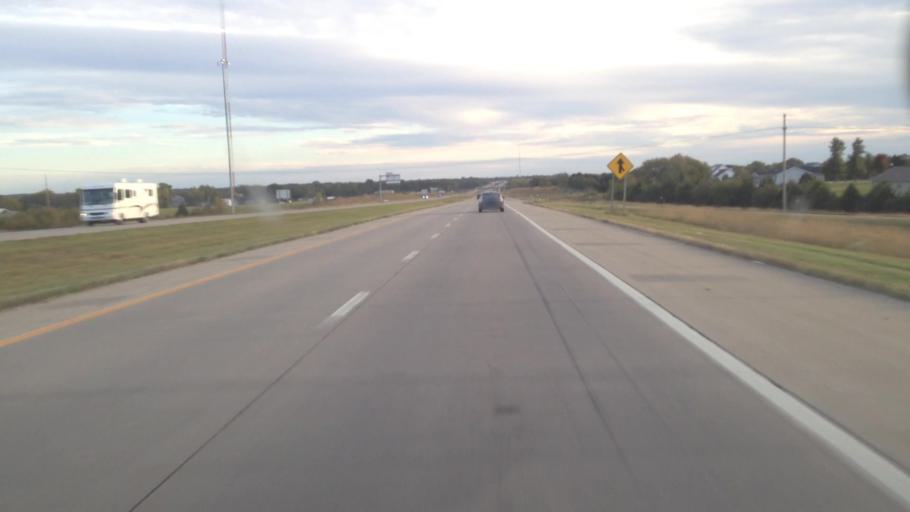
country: US
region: Kansas
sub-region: Franklin County
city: Ottawa
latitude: 38.6218
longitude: -95.2325
